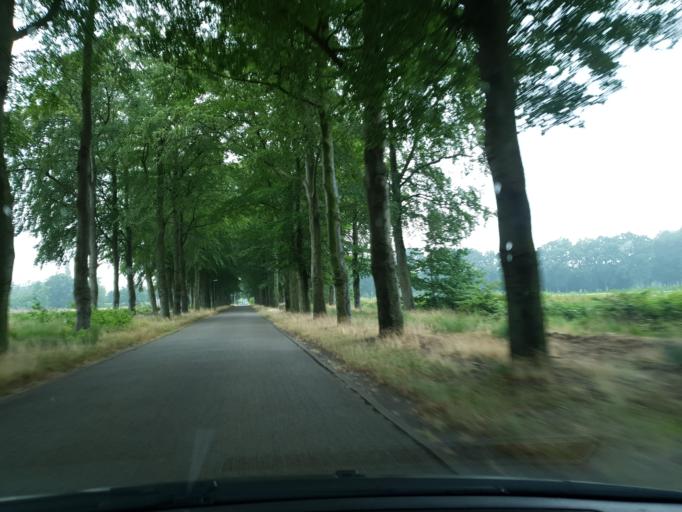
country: BE
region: Flanders
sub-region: Provincie Antwerpen
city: Merksplas
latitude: 51.3480
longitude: 4.8344
